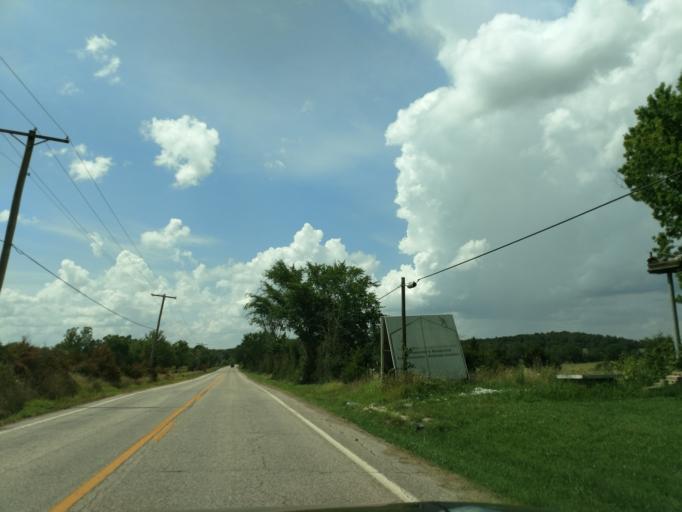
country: US
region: Arkansas
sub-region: Boone County
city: Harrison
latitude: 36.2562
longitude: -93.2249
